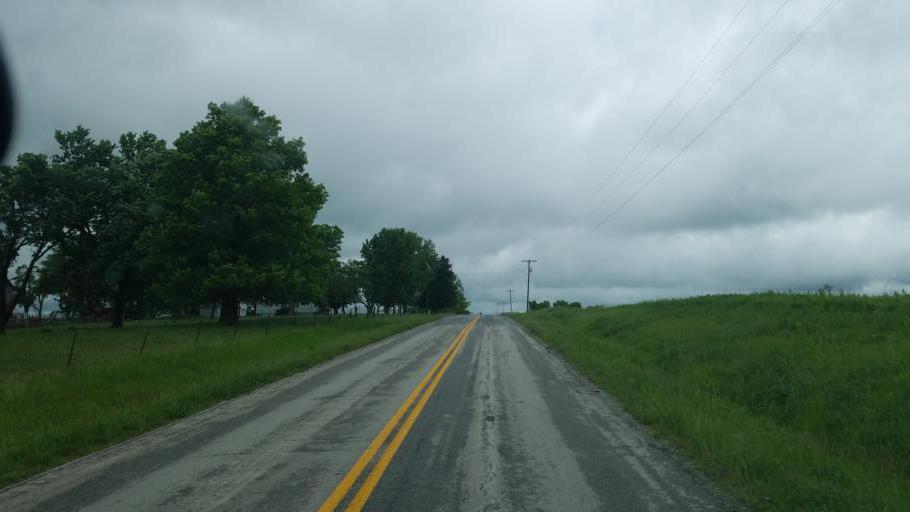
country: US
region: Missouri
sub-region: Mercer County
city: Princeton
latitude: 40.4187
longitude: -93.6848
